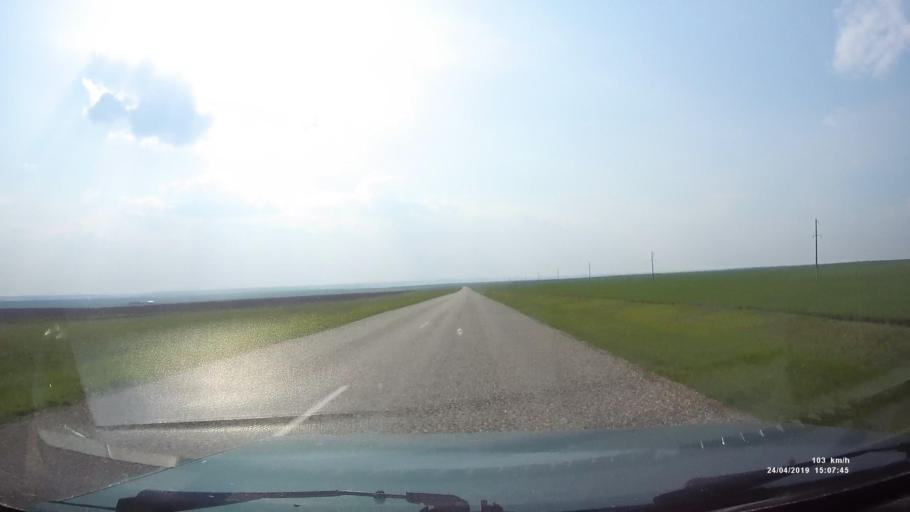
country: RU
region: Rostov
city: Remontnoye
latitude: 46.5598
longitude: 43.3982
